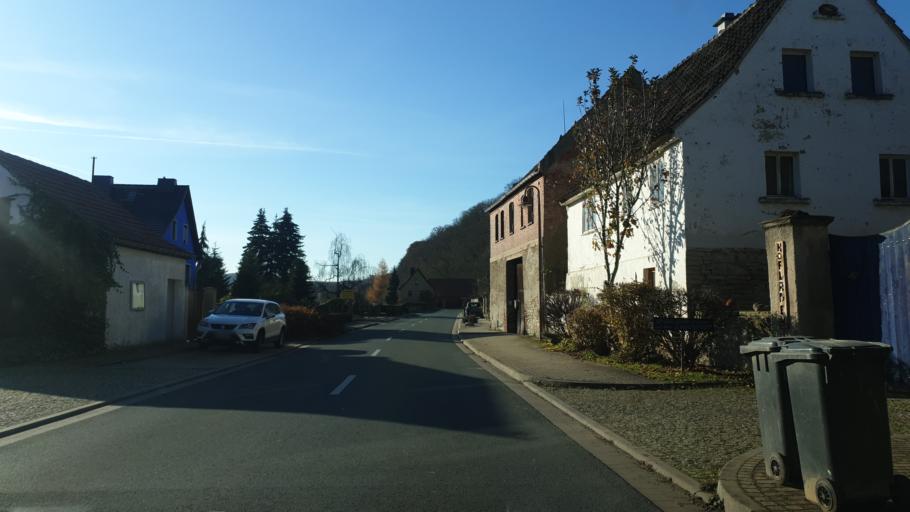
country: DE
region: Thuringia
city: Hartmannsdorf
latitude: 50.9846
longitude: 11.9874
